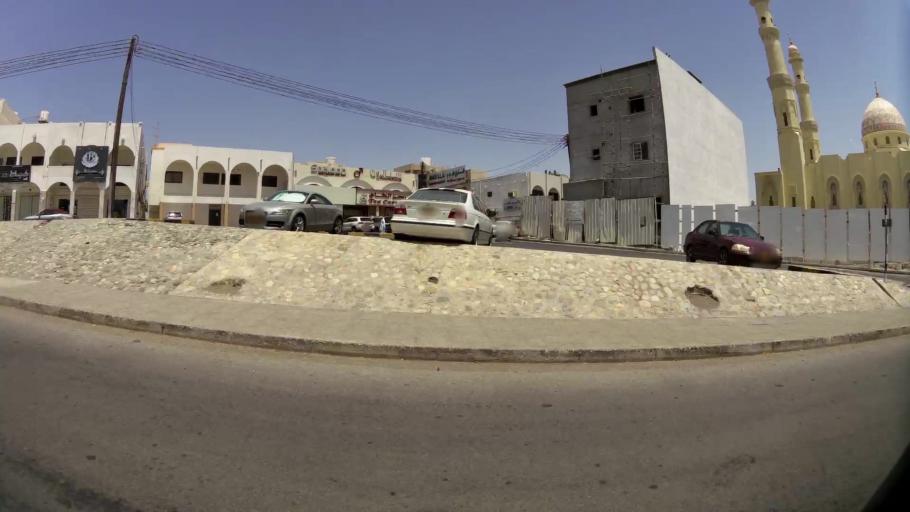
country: OM
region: Muhafazat Masqat
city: Muscat
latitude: 23.6258
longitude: 58.4860
